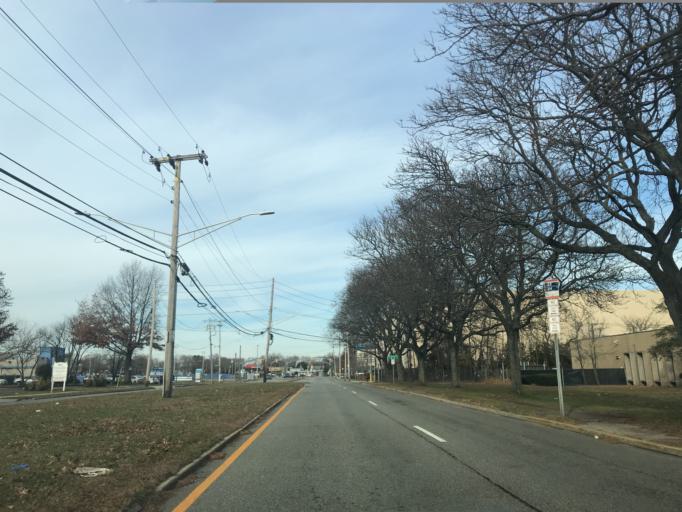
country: US
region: New York
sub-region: Nassau County
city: Carle Place
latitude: 40.7411
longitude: -73.6061
